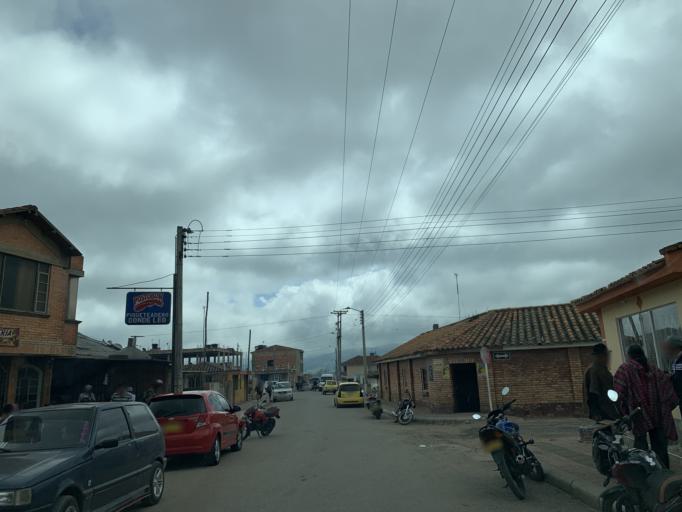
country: CO
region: Boyaca
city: Tunja
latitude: 5.5786
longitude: -73.3671
